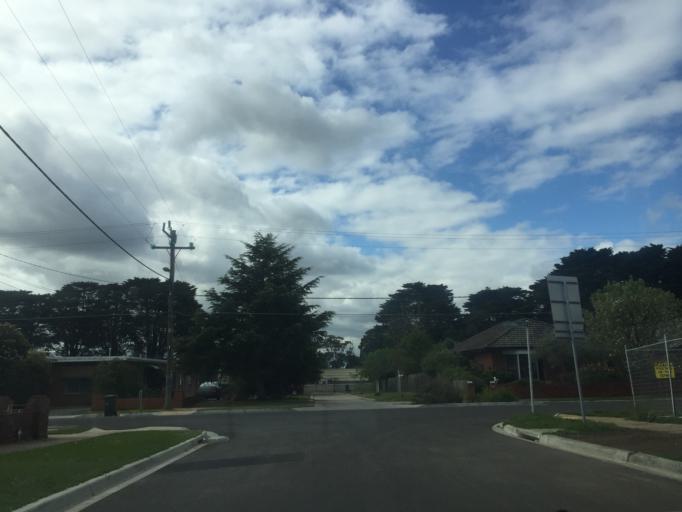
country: AU
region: Victoria
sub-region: Darebin
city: Reservoir
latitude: -37.7247
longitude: 145.0092
